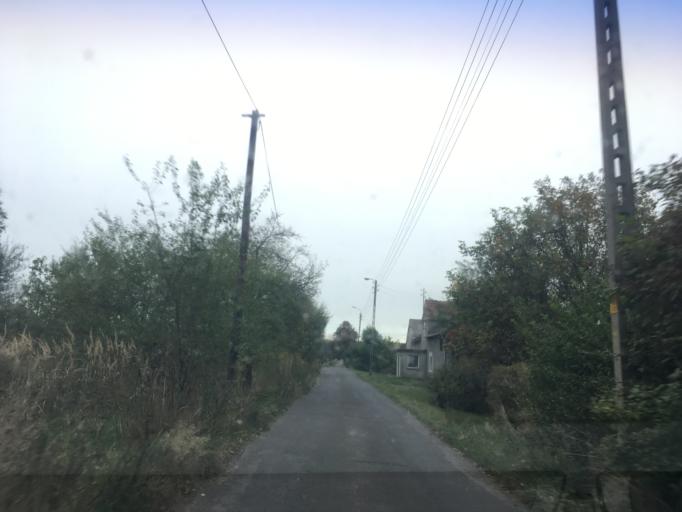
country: PL
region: Lower Silesian Voivodeship
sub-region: Powiat zgorzelecki
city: Wegliniec
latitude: 51.2334
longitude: 15.2021
